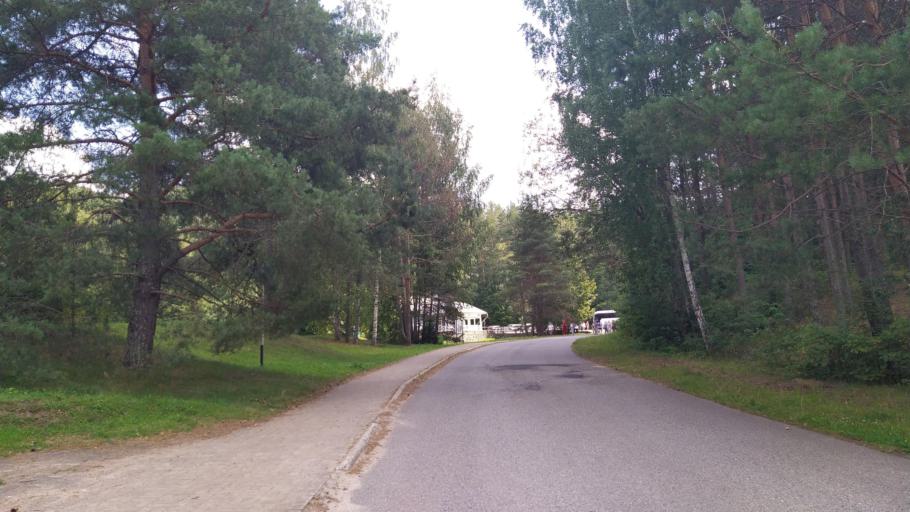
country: RU
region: Pskov
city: Pushkinskiye Gory
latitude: 57.0762
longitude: 28.9553
